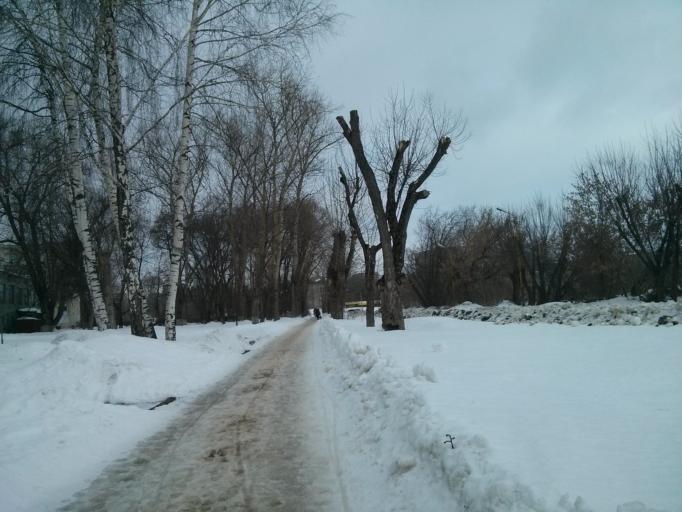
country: RU
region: Vladimir
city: Murom
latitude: 55.5620
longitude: 42.0574
